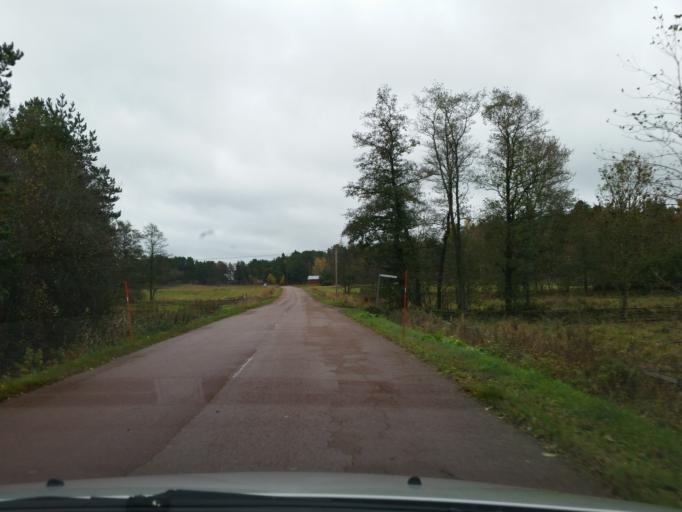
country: AX
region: Alands landsbygd
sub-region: Lumparland
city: Lumparland
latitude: 60.1321
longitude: 20.2407
